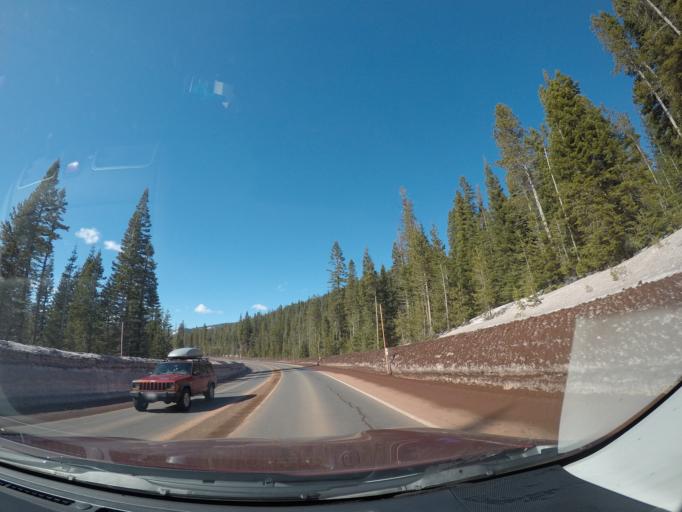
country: US
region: Oregon
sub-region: Deschutes County
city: Sunriver
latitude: 43.9822
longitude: -121.5910
